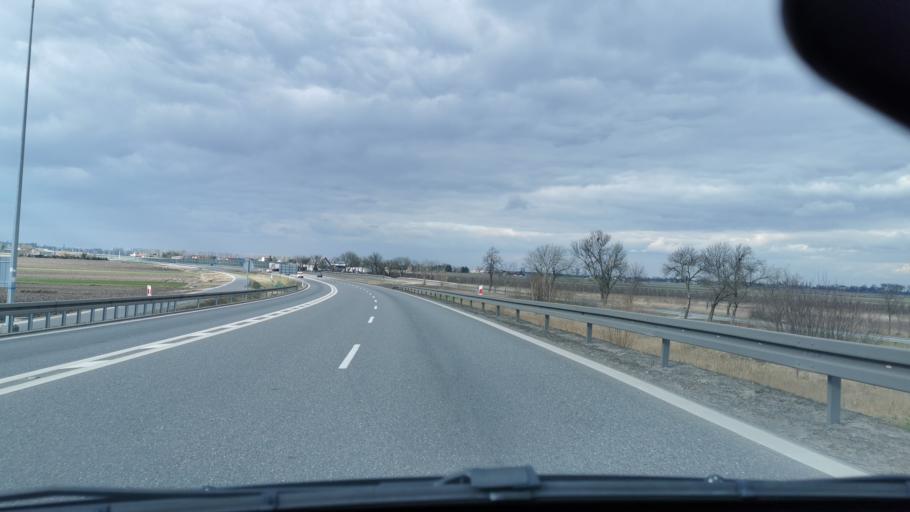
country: PL
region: Masovian Voivodeship
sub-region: Powiat zyrardowski
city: Wiskitki
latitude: 52.0927
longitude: 20.3637
